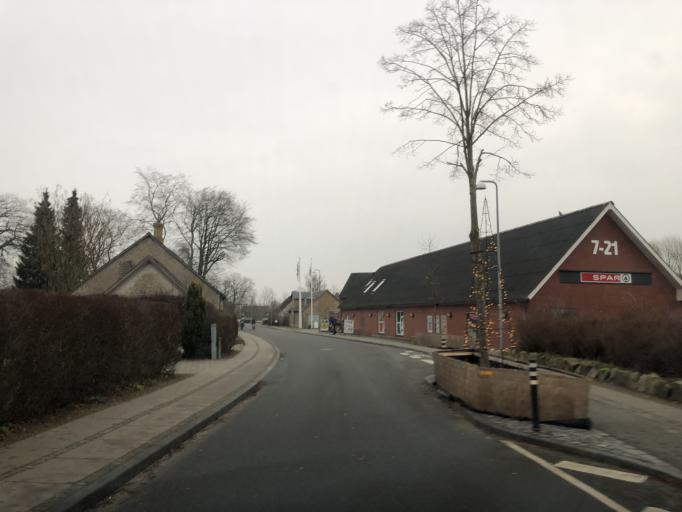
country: DK
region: South Denmark
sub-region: Faaborg-Midtfyn Kommune
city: Arslev
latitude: 55.3089
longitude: 10.4867
